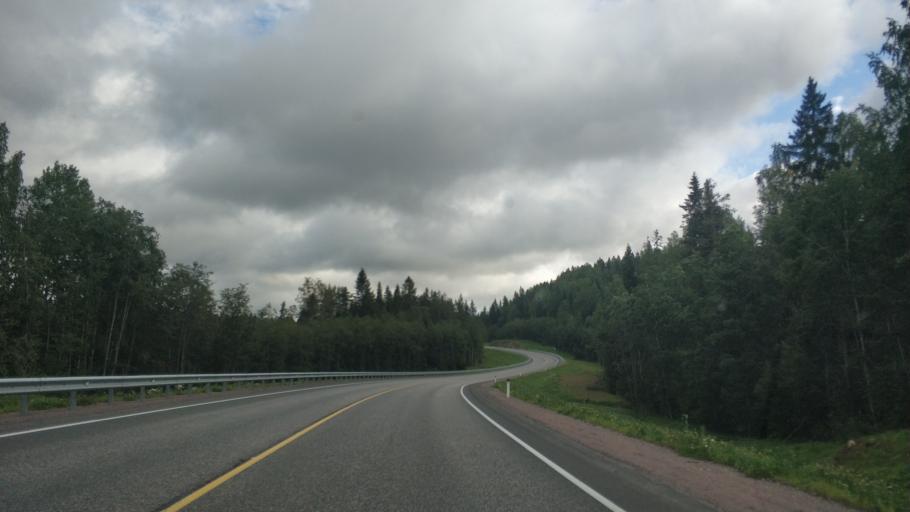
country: RU
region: Republic of Karelia
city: Khelyulya
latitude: 61.8305
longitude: 30.6357
